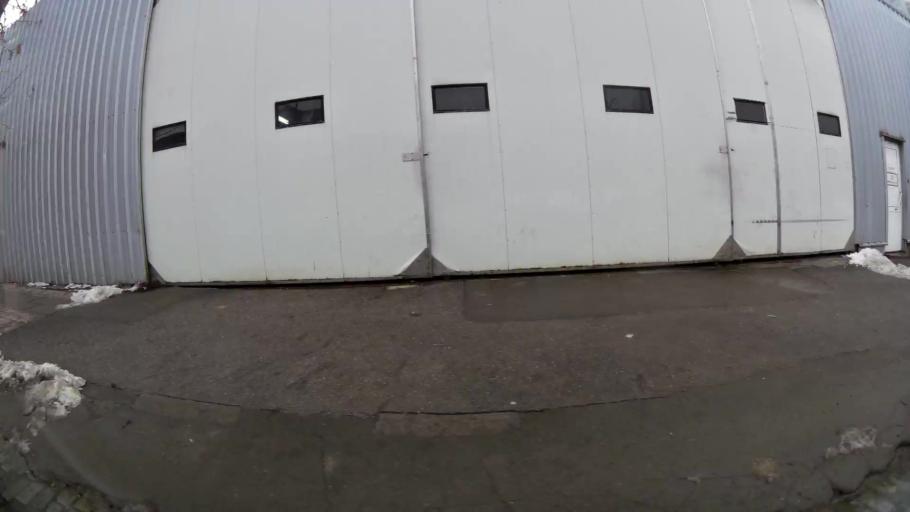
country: BG
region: Sofia-Capital
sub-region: Stolichna Obshtina
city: Sofia
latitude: 42.7068
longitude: 23.3024
